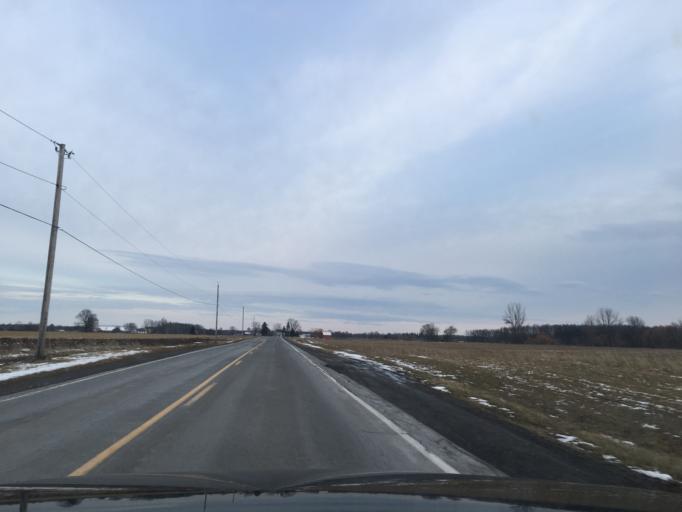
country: US
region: New York
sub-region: Ontario County
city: Manchester
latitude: 42.9557
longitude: -77.2762
